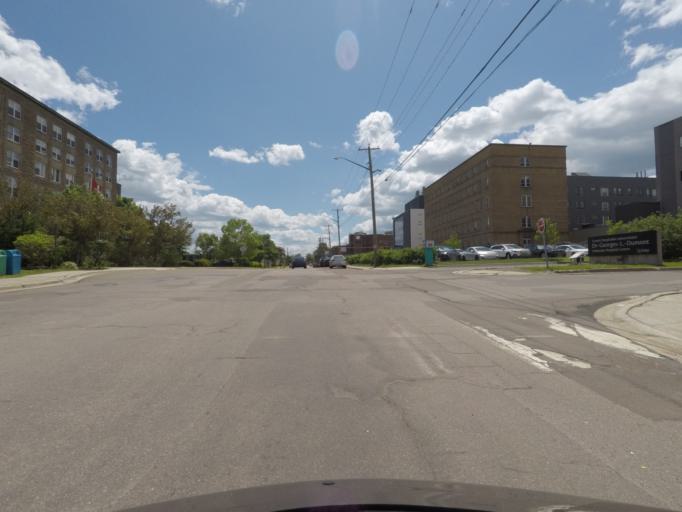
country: CA
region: New Brunswick
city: Moncton
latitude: 46.0982
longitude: -64.7861
